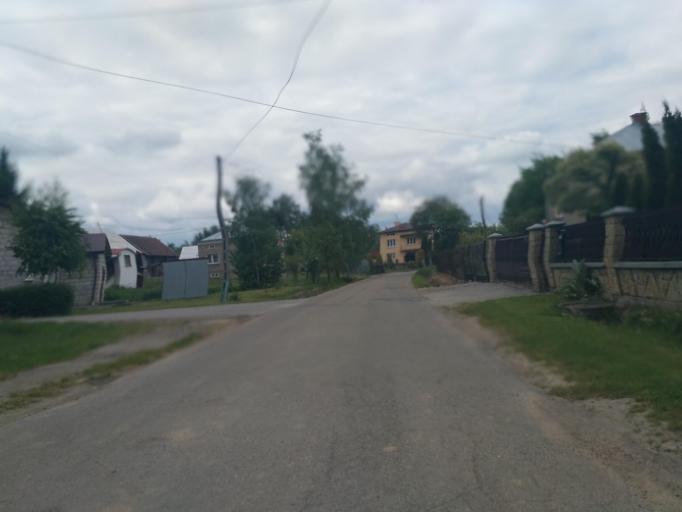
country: PL
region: Subcarpathian Voivodeship
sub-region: Powiat jasielski
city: Tarnowiec
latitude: 49.7075
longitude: 21.5818
